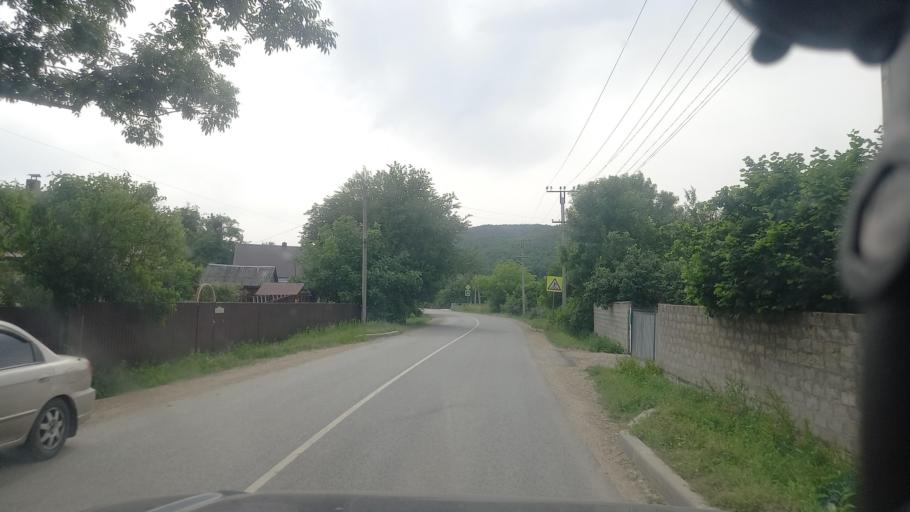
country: RU
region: Krasnodarskiy
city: Goryachiy Klyuch
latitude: 44.6053
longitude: 39.0177
